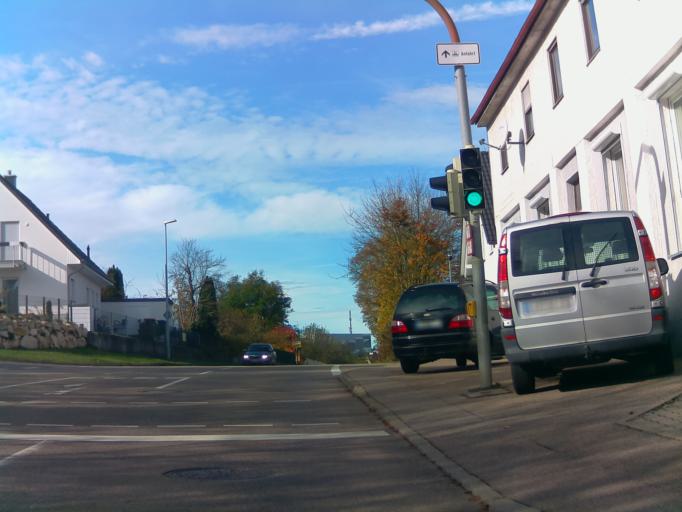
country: DE
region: Baden-Wuerttemberg
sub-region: Regierungsbezirk Stuttgart
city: Rutesheim
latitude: 48.8096
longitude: 8.9374
